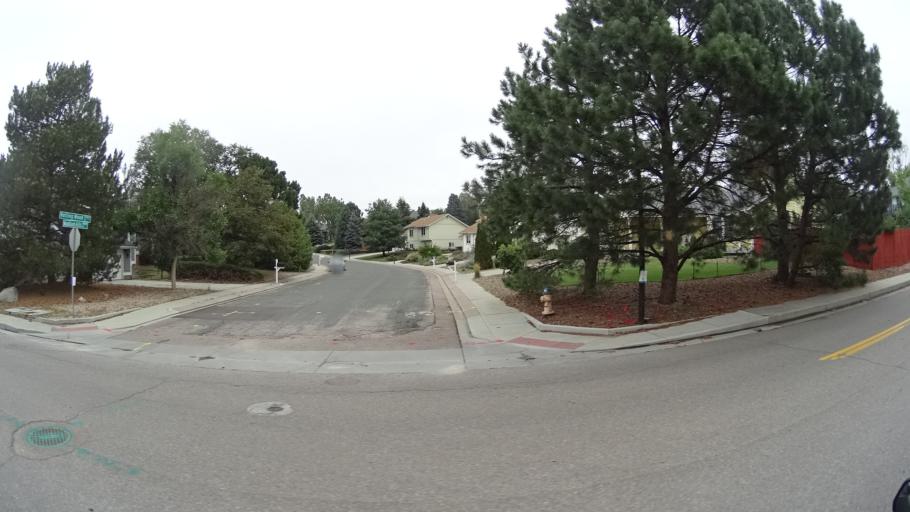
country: US
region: Colorado
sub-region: El Paso County
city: Cimarron Hills
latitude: 38.9313
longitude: -104.7695
